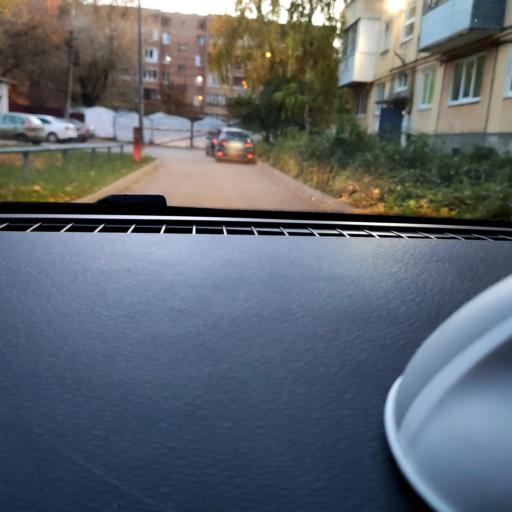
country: RU
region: Samara
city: Samara
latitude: 53.2068
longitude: 50.1827
